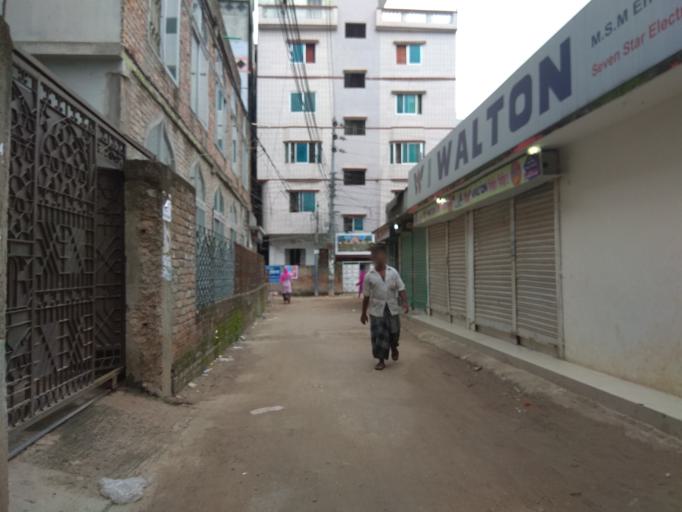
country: BD
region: Dhaka
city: Azimpur
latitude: 23.7967
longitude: 90.3689
